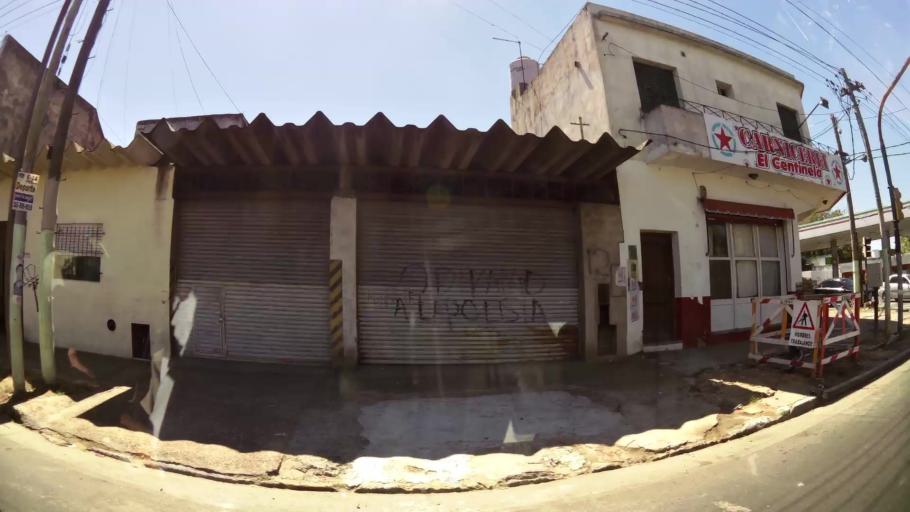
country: AR
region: Buenos Aires
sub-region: Partido de Quilmes
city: Quilmes
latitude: -34.7227
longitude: -58.2877
